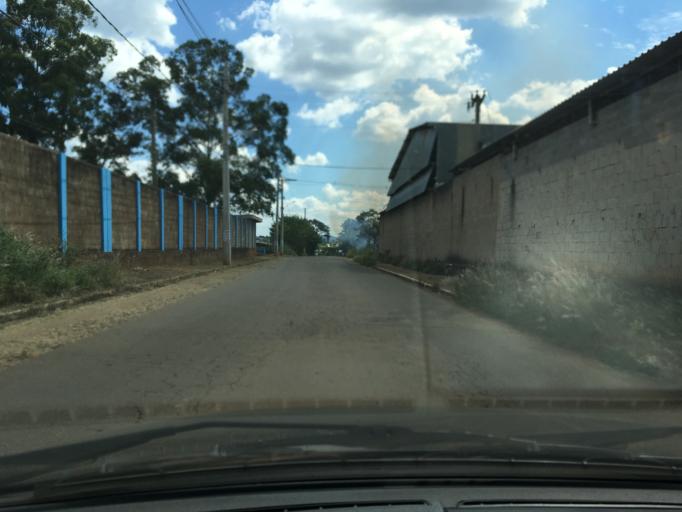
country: BR
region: Minas Gerais
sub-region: Mateus Leme
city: Mateus Leme
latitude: -19.9968
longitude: -44.4382
